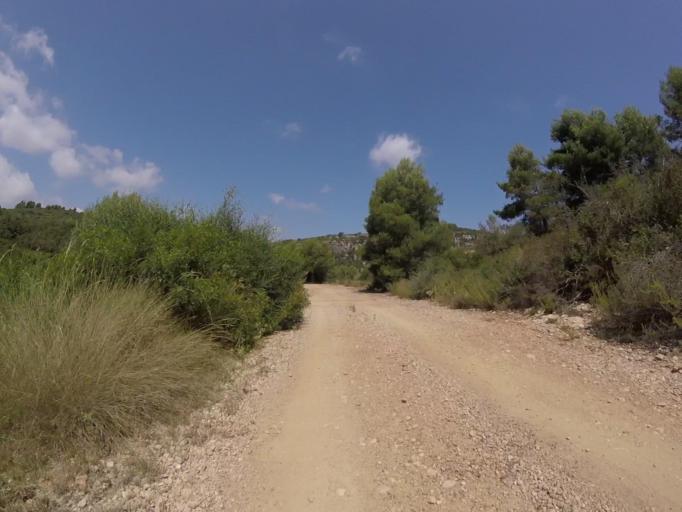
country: ES
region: Valencia
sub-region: Provincia de Castello
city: Torreblanca
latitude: 40.2198
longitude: 0.1487
